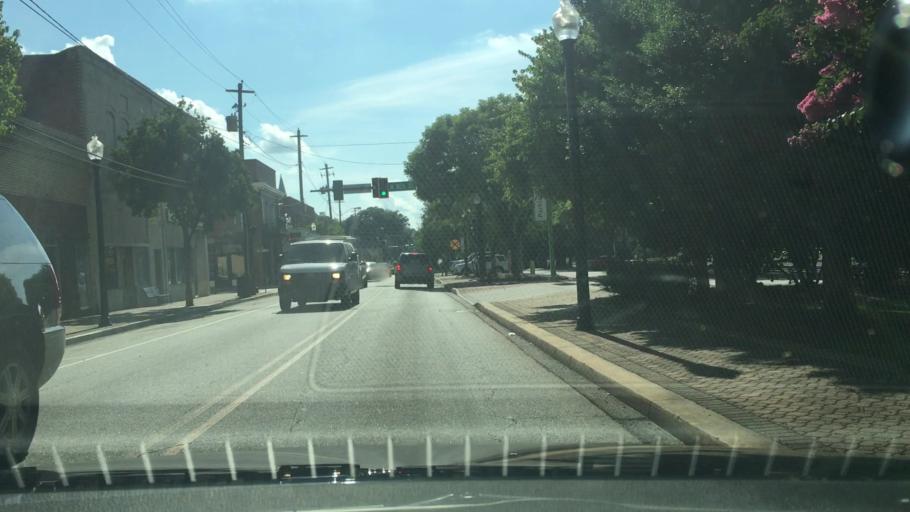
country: US
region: Georgia
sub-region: Spalding County
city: Griffin
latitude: 33.2501
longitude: -84.2648
